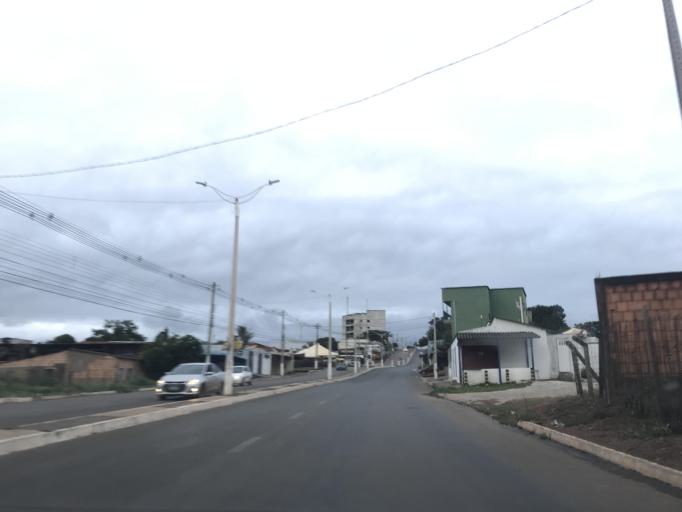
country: BR
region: Goias
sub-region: Luziania
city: Luziania
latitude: -16.2431
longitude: -47.9453
